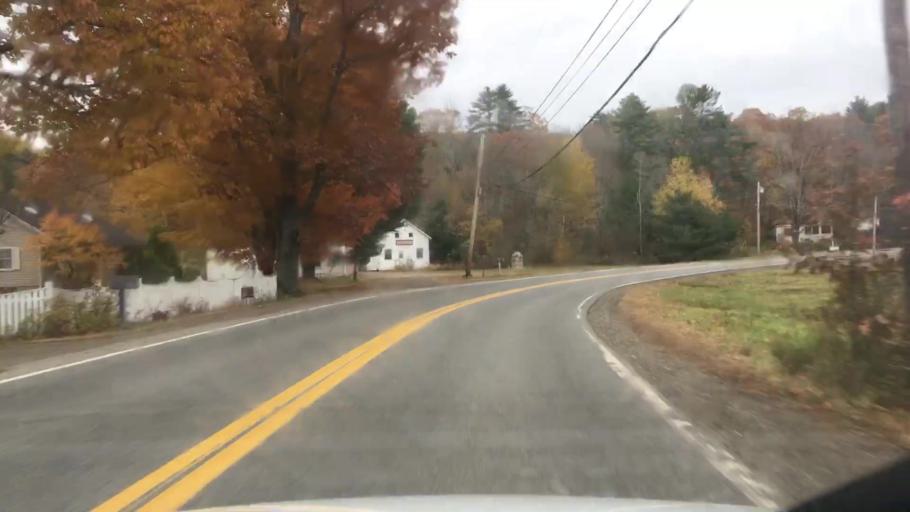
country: US
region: Maine
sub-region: Lincoln County
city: Jefferson
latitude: 44.2003
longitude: -69.4535
